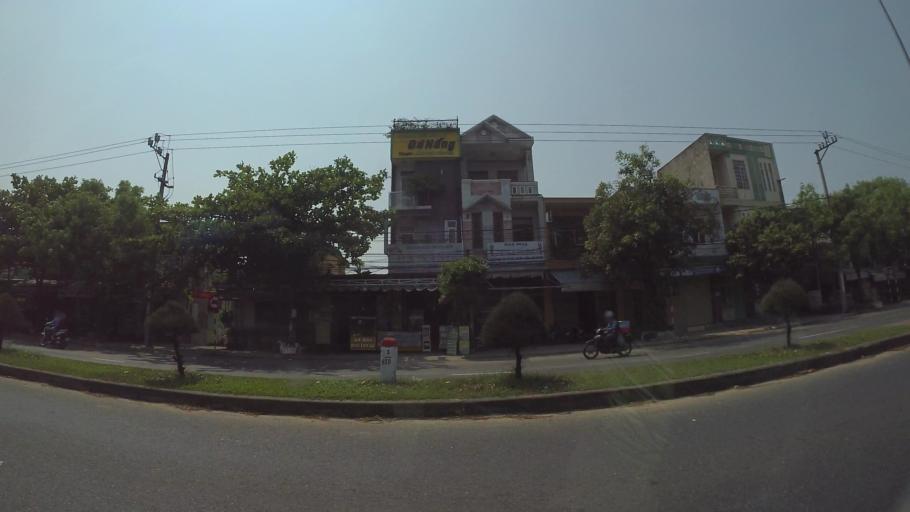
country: VN
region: Da Nang
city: Cam Le
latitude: 15.9794
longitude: 108.2084
